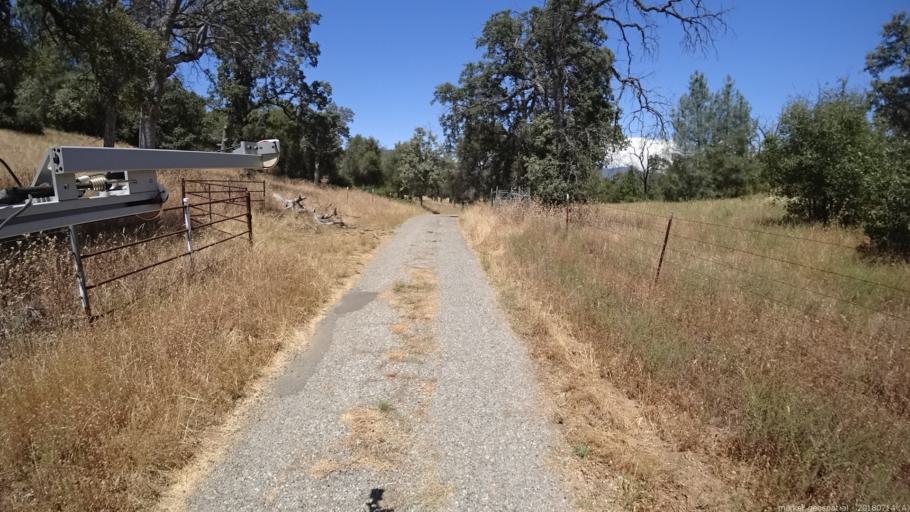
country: US
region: California
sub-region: Madera County
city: Ahwahnee
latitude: 37.3875
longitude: -119.7591
